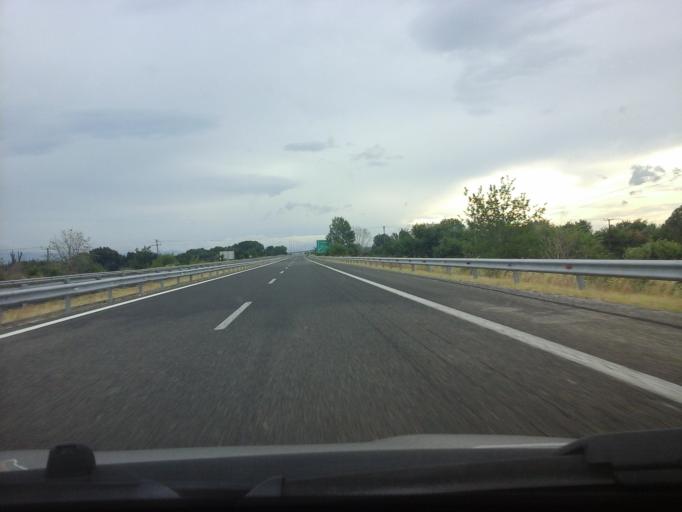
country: GR
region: East Macedonia and Thrace
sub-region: Nomos Rodopis
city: Komotini
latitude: 41.0955
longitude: 25.4166
